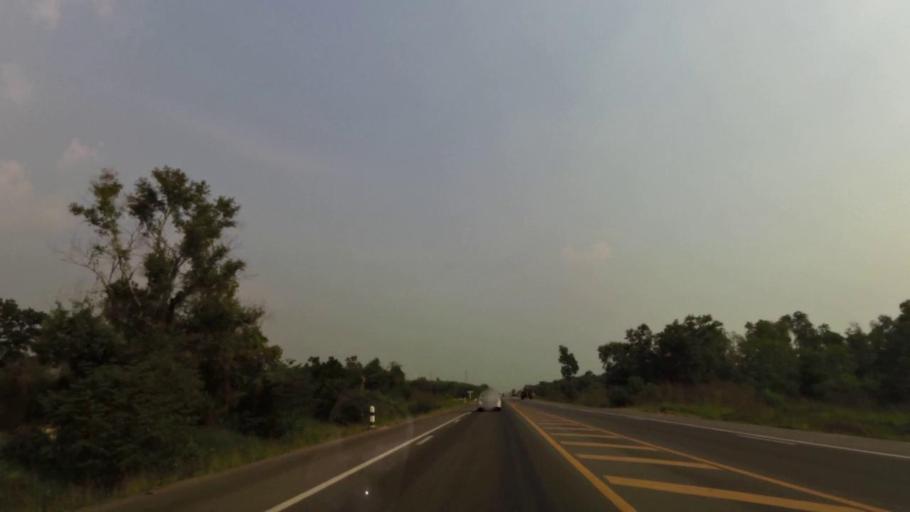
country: TH
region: Rayong
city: Klaeng
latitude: 12.8071
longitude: 101.6501
